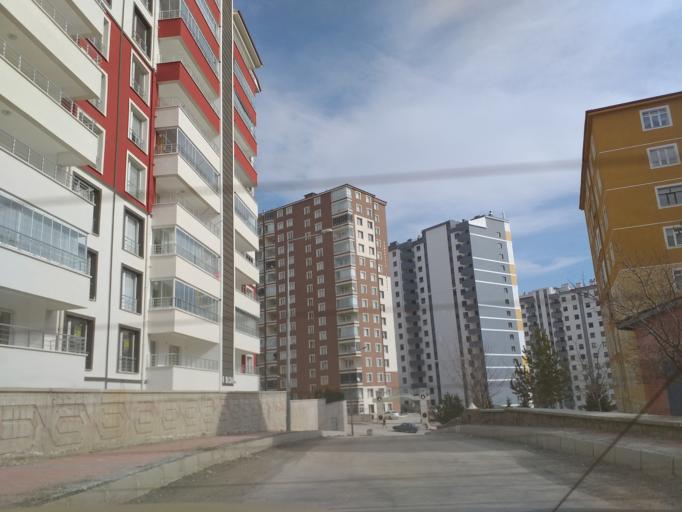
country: TR
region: Yozgat
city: Yozgat
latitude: 39.8317
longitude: 34.8216
